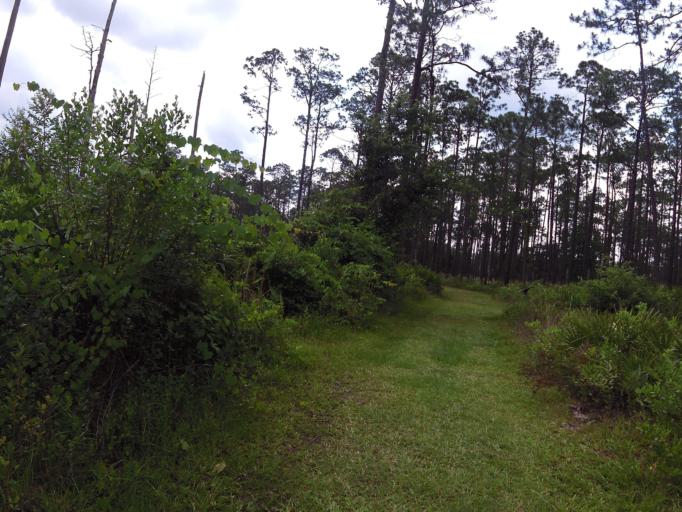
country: US
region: Florida
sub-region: Union County
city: Lake Butler
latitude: 30.2156
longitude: -82.3887
